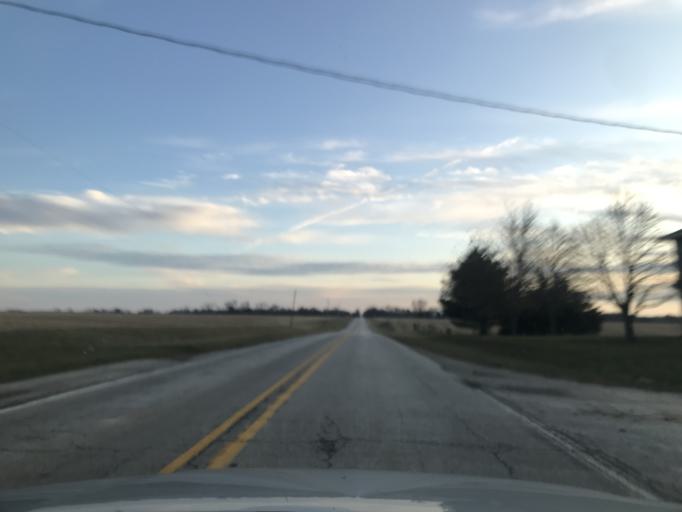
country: US
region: Illinois
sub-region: Henderson County
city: Oquawka
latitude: 40.9686
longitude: -90.8639
